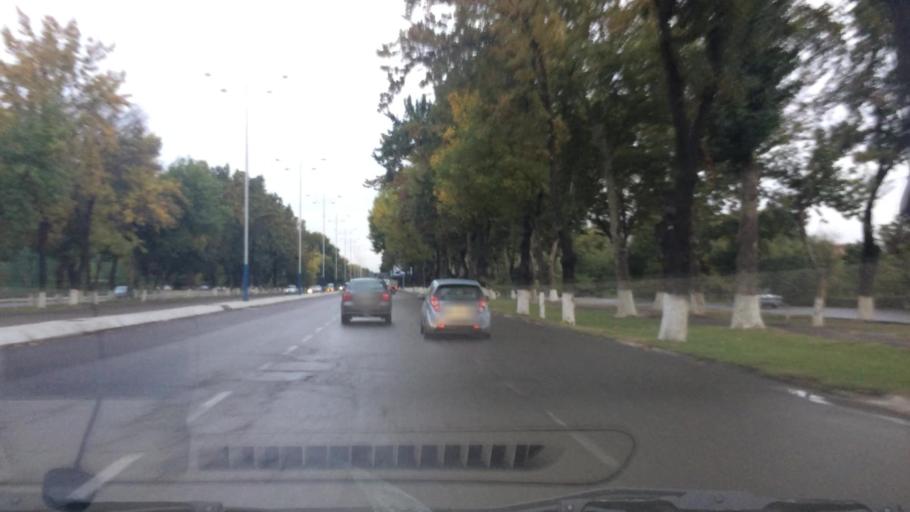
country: UZ
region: Toshkent Shahri
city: Tashkent
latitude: 41.2631
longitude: 69.1980
